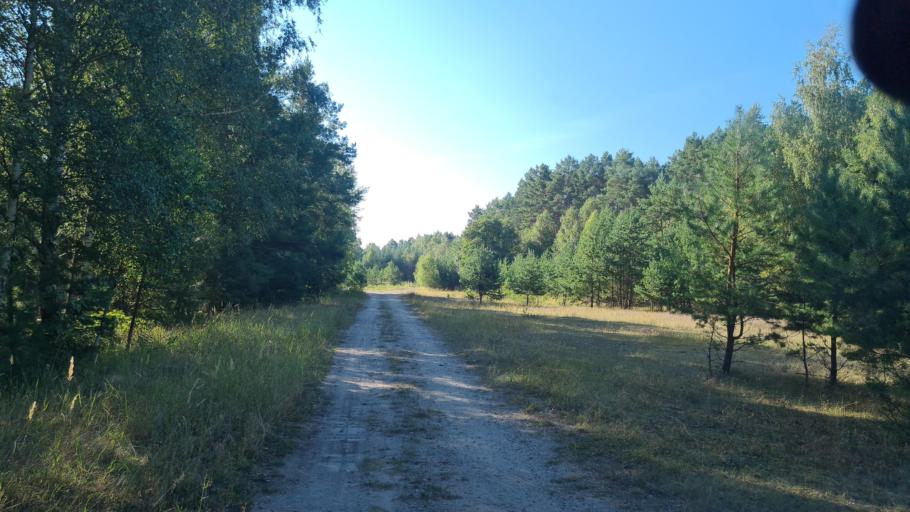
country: DE
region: Brandenburg
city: Schonborn
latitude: 51.6387
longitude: 13.5124
